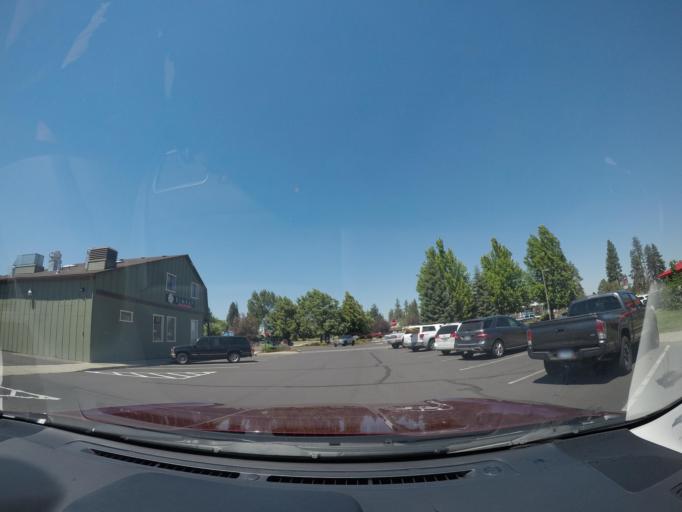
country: US
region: Oregon
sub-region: Deschutes County
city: Sisters
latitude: 44.2901
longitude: -121.5451
